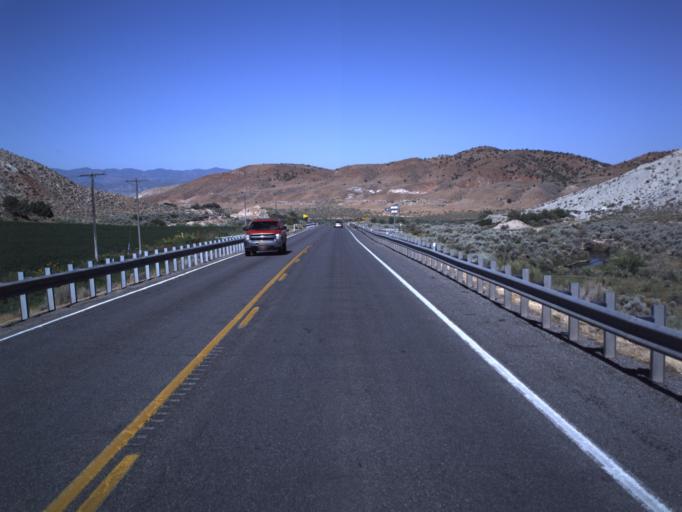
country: US
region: Utah
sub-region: Sanpete County
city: Gunnison
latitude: 39.1686
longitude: -111.7157
